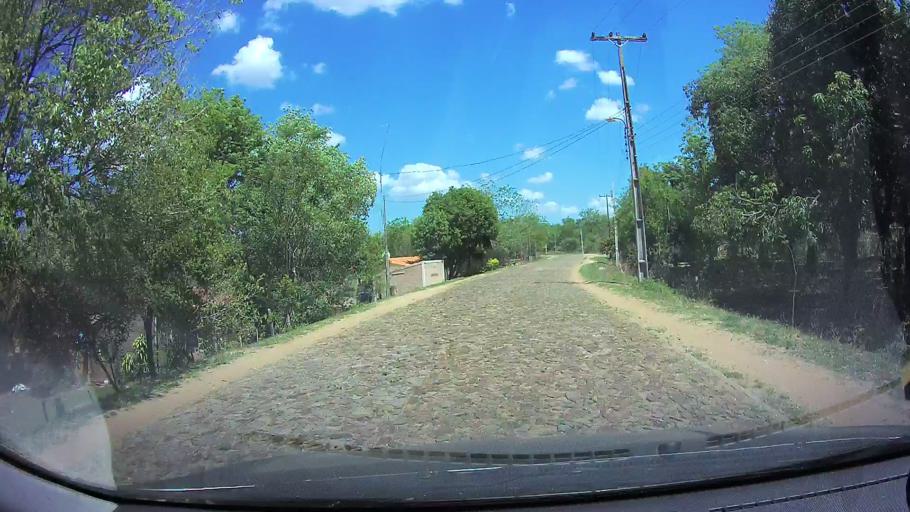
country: PY
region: Cordillera
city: Emboscada
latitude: -25.1163
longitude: -57.3086
